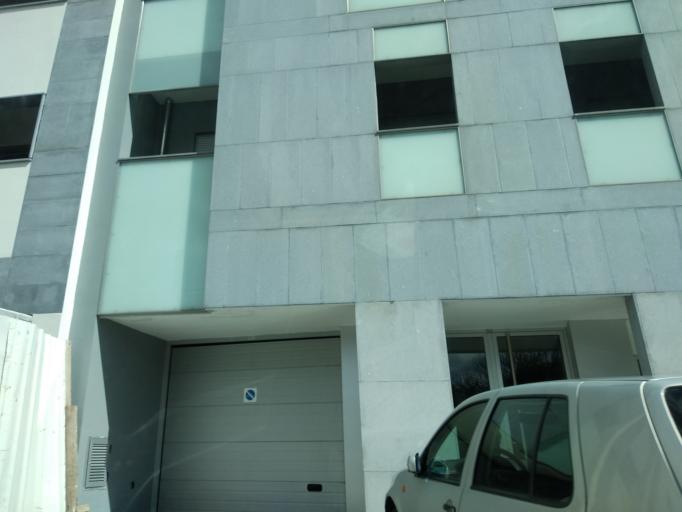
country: PT
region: Braga
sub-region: Braga
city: Braga
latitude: 41.5546
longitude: -8.4138
